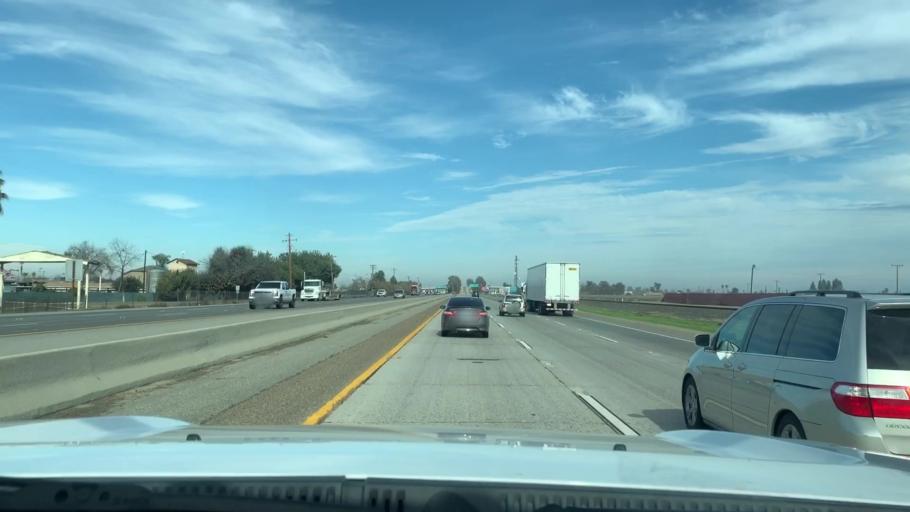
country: US
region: California
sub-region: Kern County
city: McFarland
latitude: 35.6652
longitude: -119.2241
